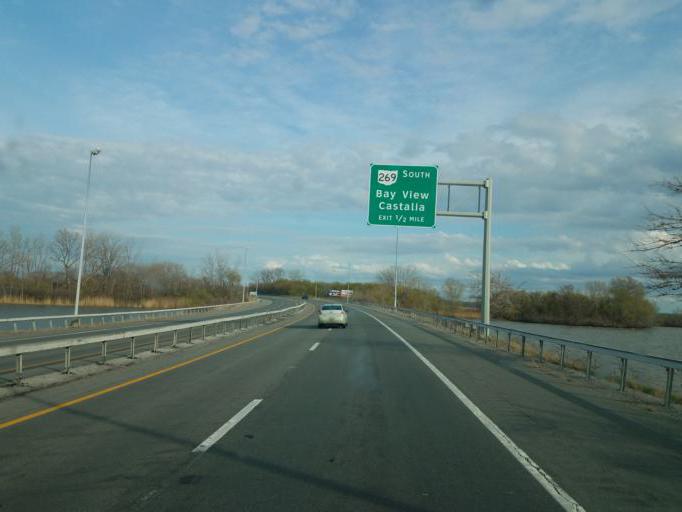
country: US
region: Ohio
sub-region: Ottawa County
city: Port Clinton
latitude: 41.4634
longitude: -82.8304
